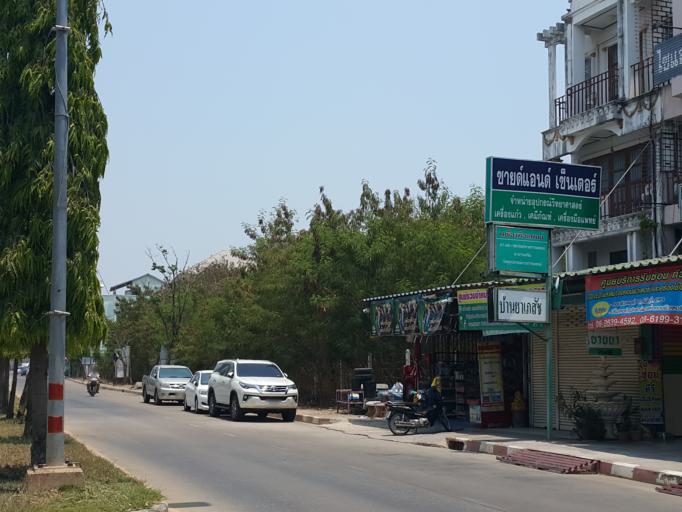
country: TH
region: Phitsanulok
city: Phitsanulok
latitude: 16.8189
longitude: 100.2454
